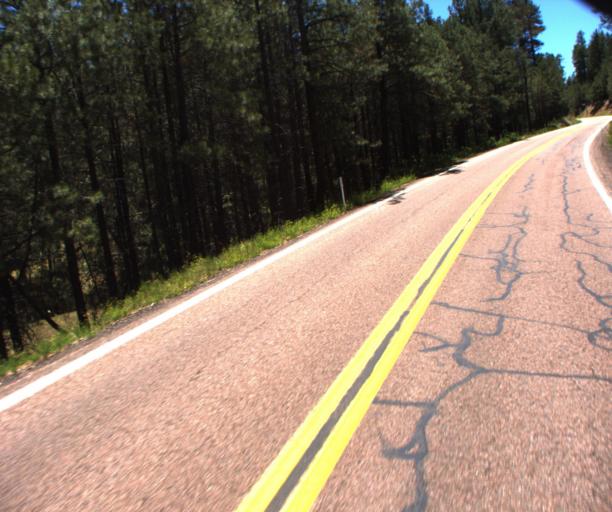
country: US
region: Arizona
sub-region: Gila County
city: Pine
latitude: 34.4966
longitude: -111.3687
